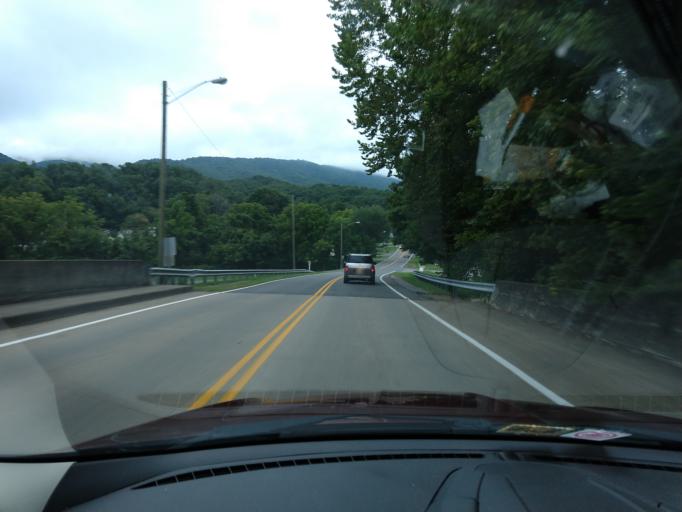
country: US
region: Virginia
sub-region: City of Covington
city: Fairlawn
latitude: 37.7564
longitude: -79.9869
